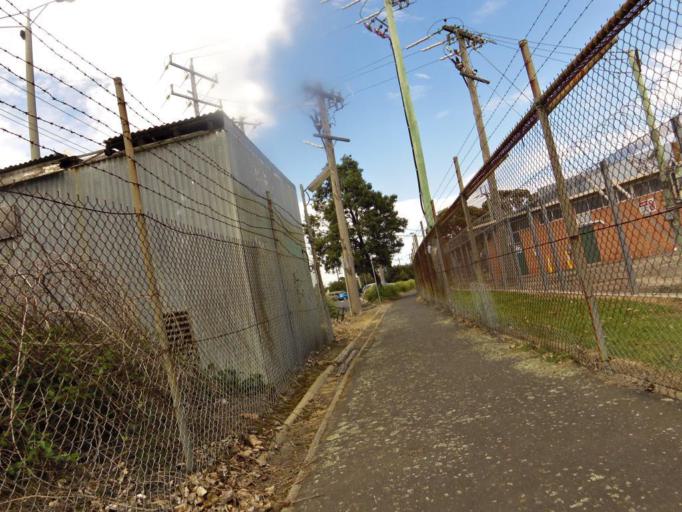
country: AU
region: Victoria
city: Carnegie
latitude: -37.8784
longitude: 145.0707
